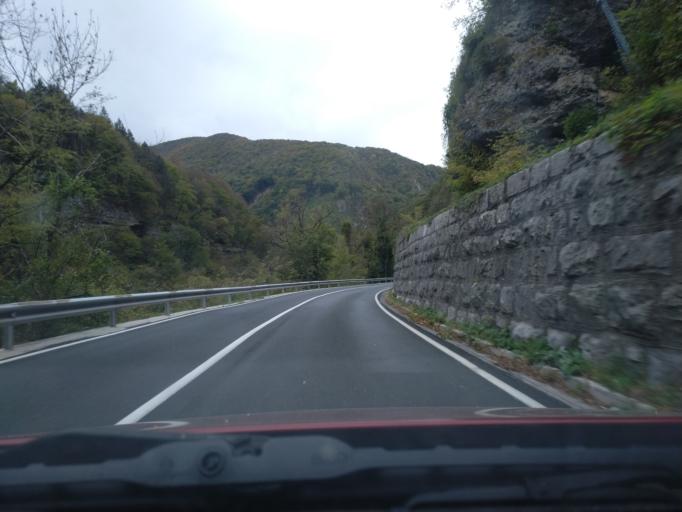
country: SI
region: Tolmin
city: Tolmin
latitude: 46.1308
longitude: 13.7151
